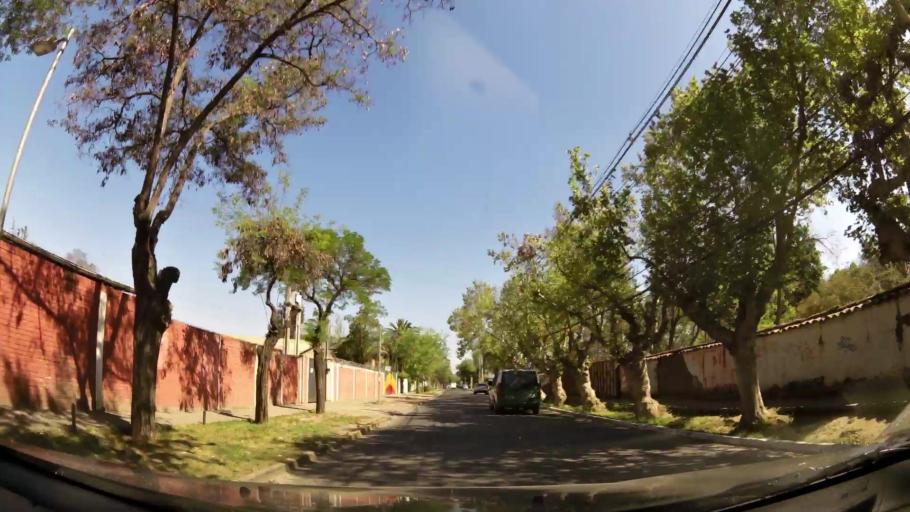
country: CL
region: Santiago Metropolitan
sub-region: Provincia de Maipo
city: San Bernardo
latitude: -33.5924
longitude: -70.7096
